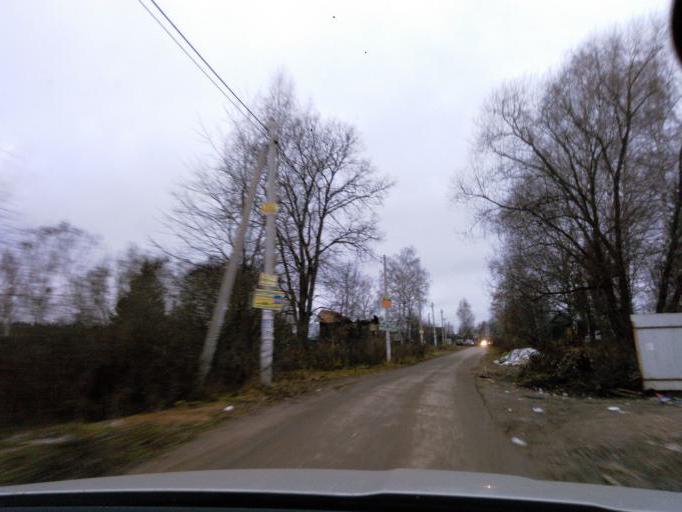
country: RU
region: Moskovskaya
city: Lozhki
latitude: 56.0588
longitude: 37.1014
